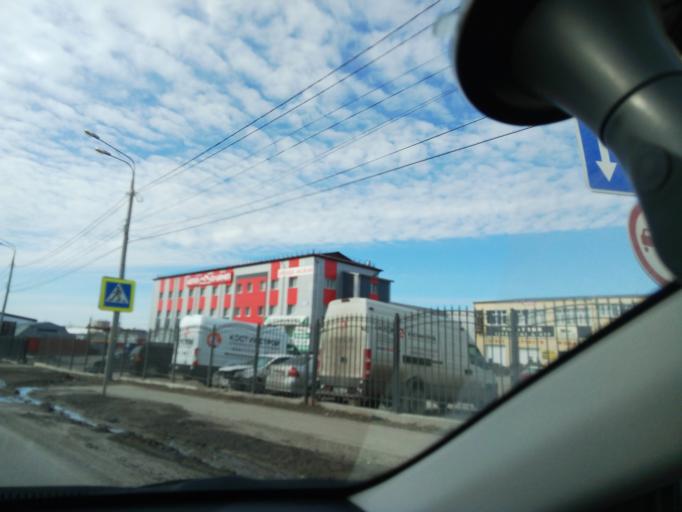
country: RU
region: Chuvashia
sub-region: Cheboksarskiy Rayon
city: Cheboksary
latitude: 56.1051
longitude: 47.2519
